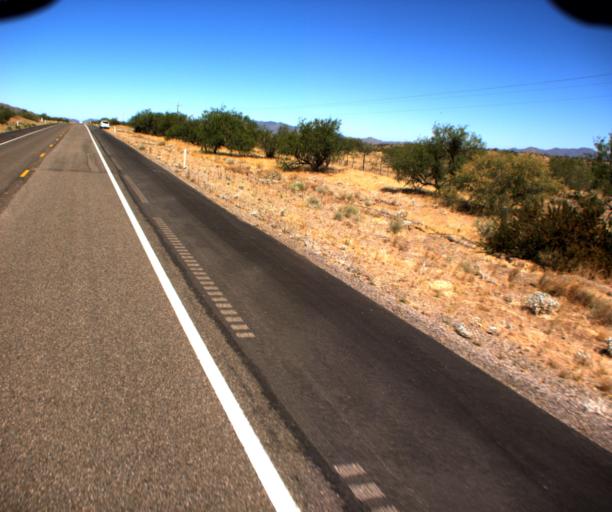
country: US
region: Arizona
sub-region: Pima County
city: Three Points
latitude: 32.0228
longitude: -111.5984
